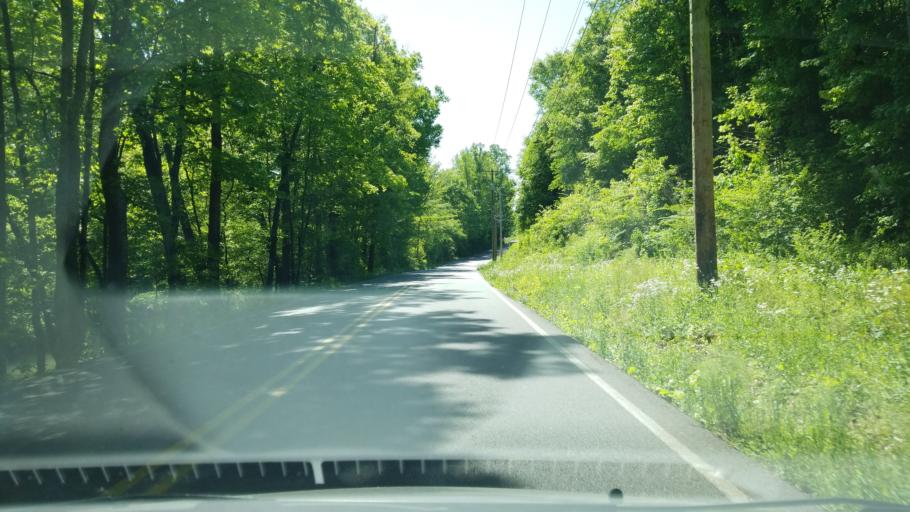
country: US
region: Tennessee
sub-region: Hamilton County
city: Falling Water
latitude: 35.1798
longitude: -85.2385
